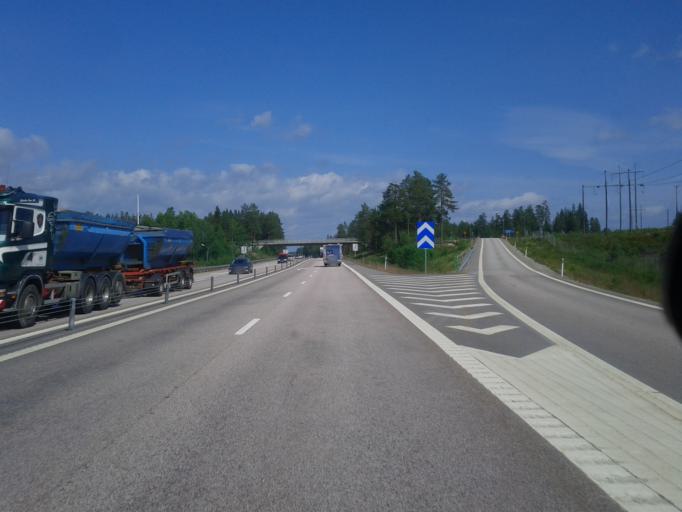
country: SE
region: Vaesterbotten
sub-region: Nordmalings Kommun
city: Nordmaling
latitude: 63.5347
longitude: 19.4000
